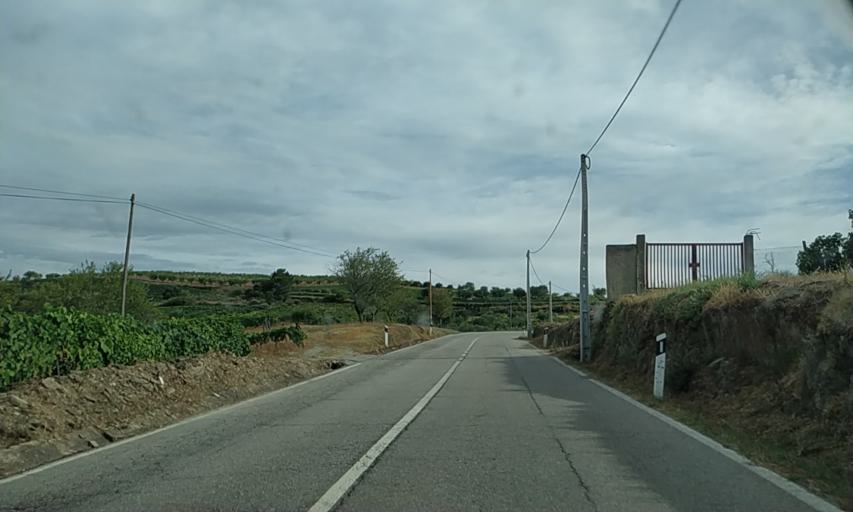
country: PT
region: Viseu
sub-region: Sao Joao da Pesqueira
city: Sao Joao da Pesqueira
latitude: 41.0770
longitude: -7.3905
